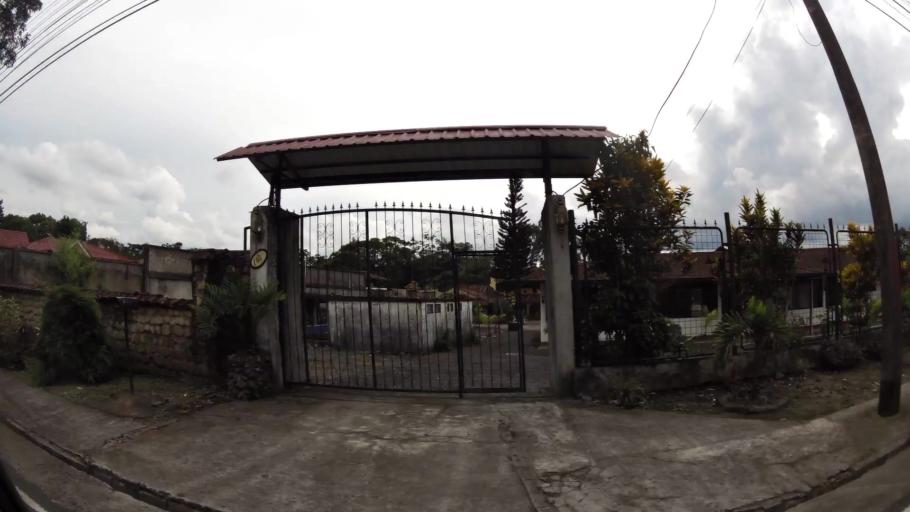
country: EC
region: Pastaza
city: Puyo
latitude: -1.5068
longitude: -78.0342
